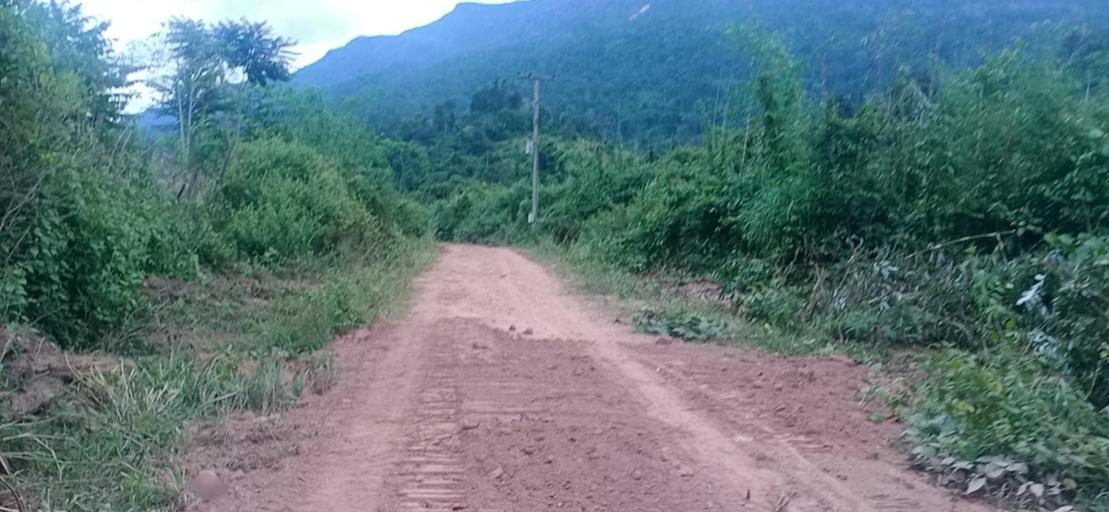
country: TH
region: Changwat Bueng Kan
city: Pak Khat
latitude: 18.5585
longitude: 103.2354
